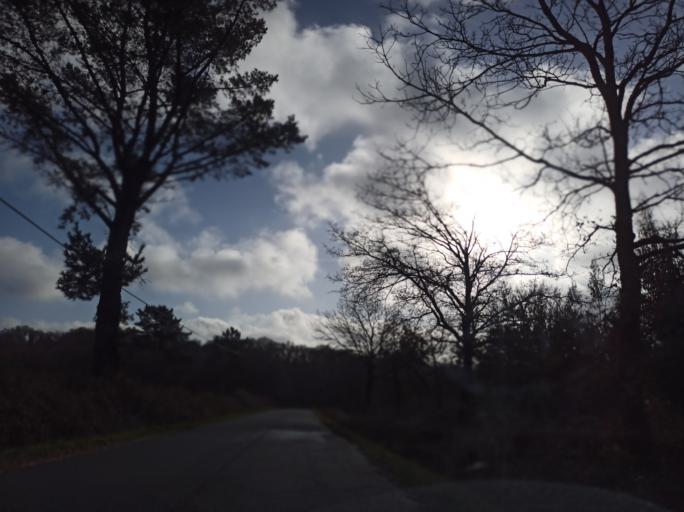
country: ES
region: Galicia
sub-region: Provincia da Coruna
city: Sobrado
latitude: 43.0923
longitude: -7.9716
